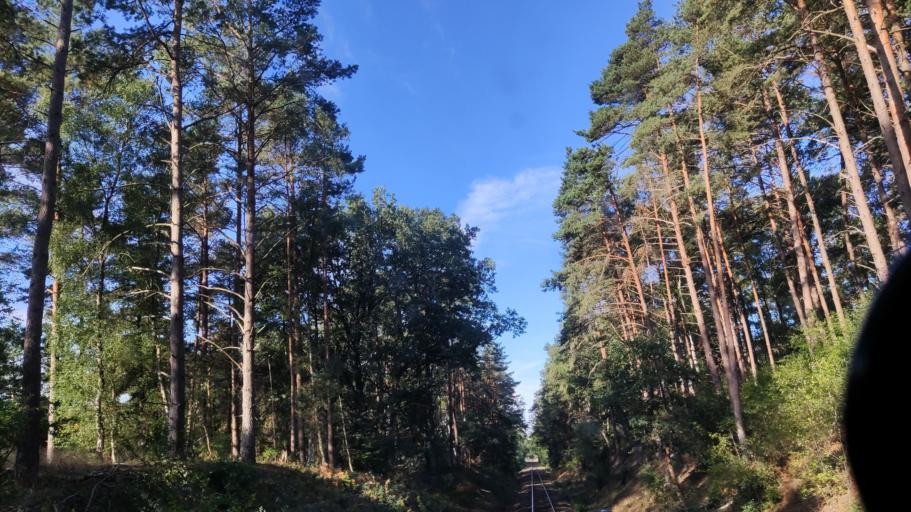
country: DE
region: Lower Saxony
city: Amelinghausen
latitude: 53.1328
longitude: 10.2560
